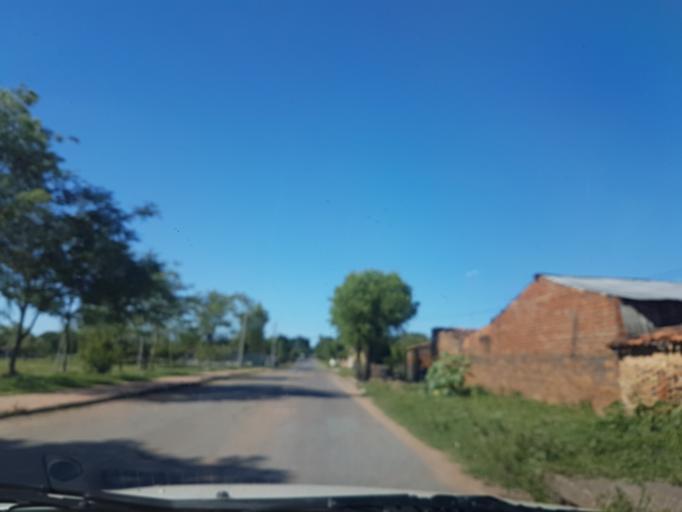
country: PY
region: Cordillera
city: Tobati
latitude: -25.2637
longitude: -57.0870
